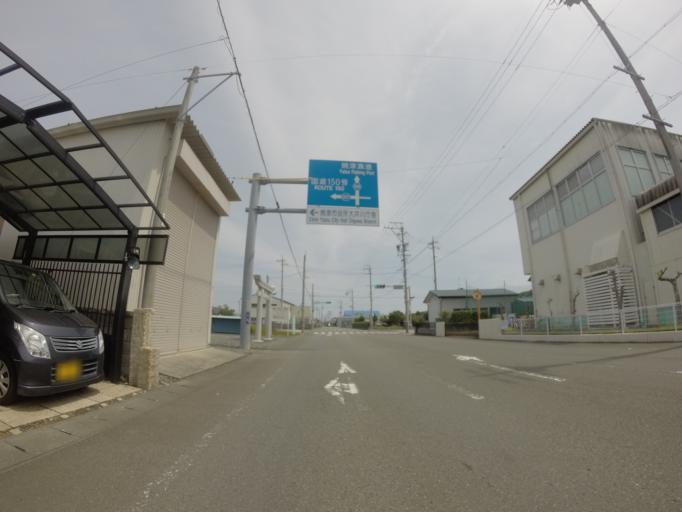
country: JP
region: Shizuoka
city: Yaizu
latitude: 34.7909
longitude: 138.3045
